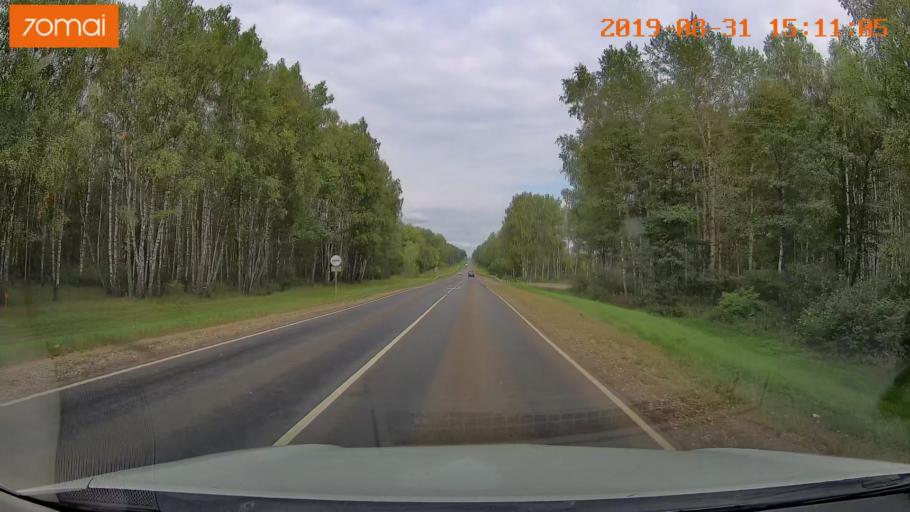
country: RU
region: Kaluga
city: Spas-Demensk
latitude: 54.4195
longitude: 34.2350
